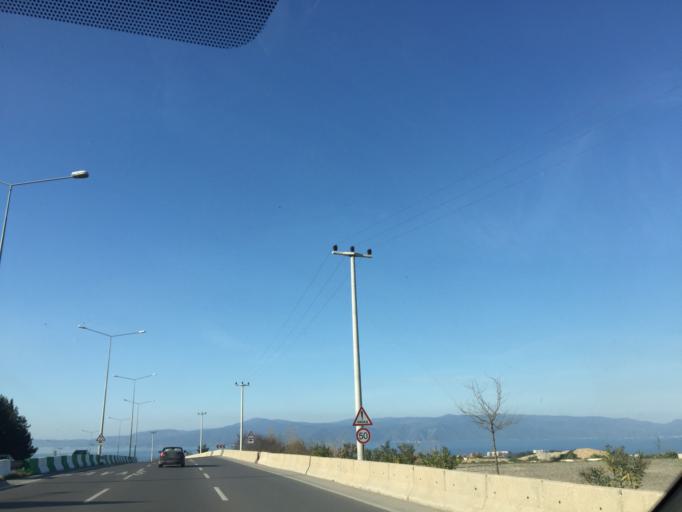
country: TR
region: Bursa
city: Niluefer
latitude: 40.3227
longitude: 28.9319
